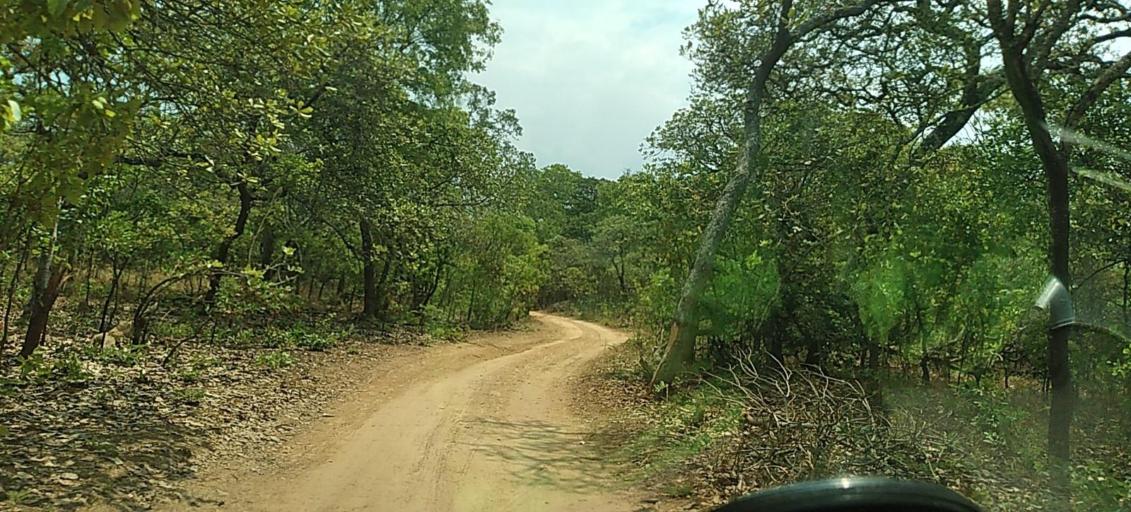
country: ZM
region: North-Western
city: Kansanshi
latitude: -12.0116
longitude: 26.2554
